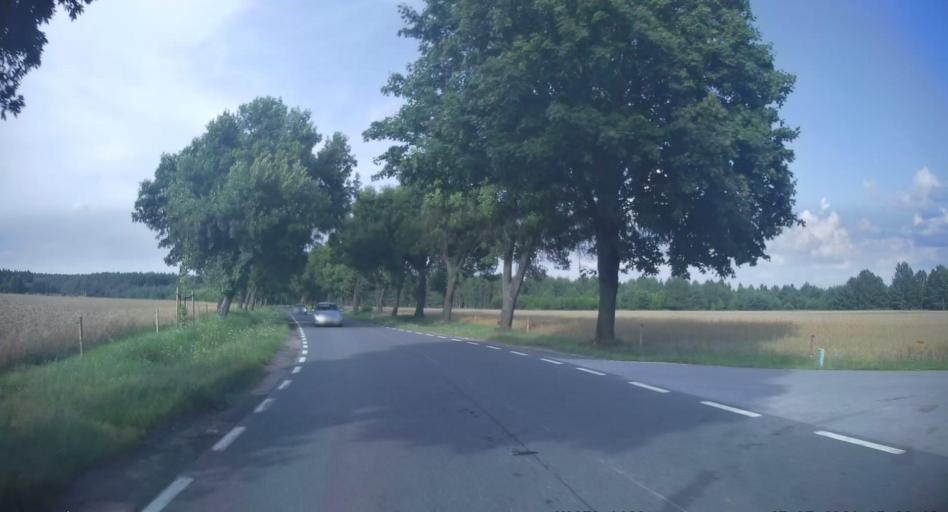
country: PL
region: Lodz Voivodeship
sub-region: Powiat tomaszowski
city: Inowlodz
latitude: 51.5339
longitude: 20.2301
